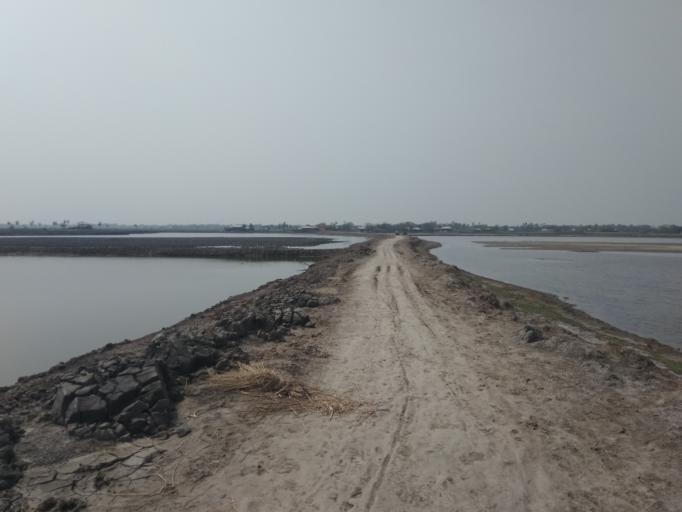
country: IN
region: West Bengal
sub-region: North 24 Parganas
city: Taki
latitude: 22.3466
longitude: 89.2264
